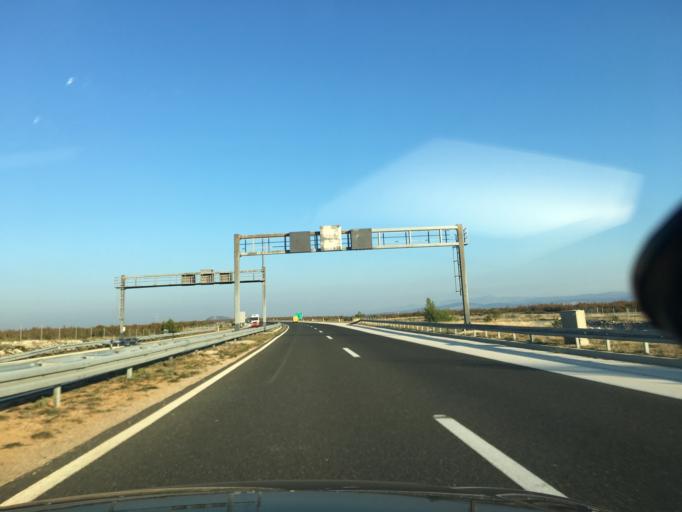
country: HR
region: Sibensko-Kniniska
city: Zaton
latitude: 43.8945
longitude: 15.7840
